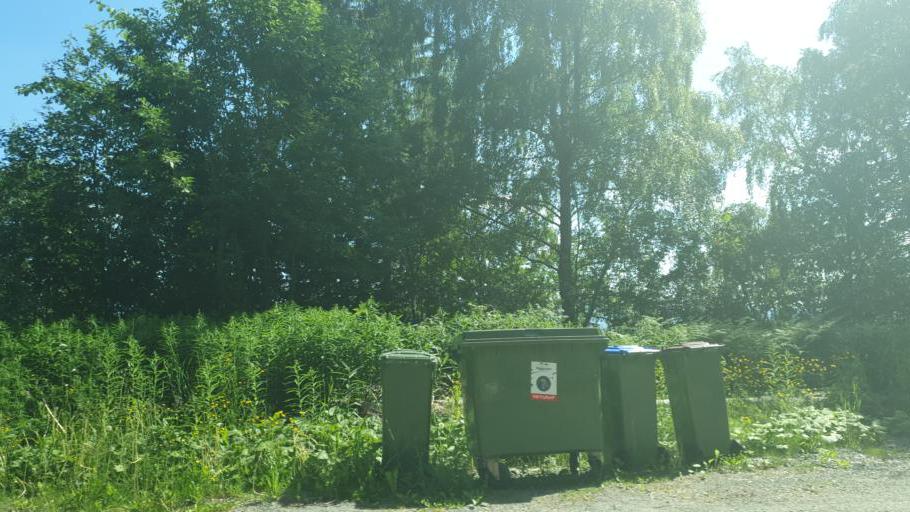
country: NO
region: Nord-Trondelag
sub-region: Frosta
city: Frosta
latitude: 63.7075
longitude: 10.7649
